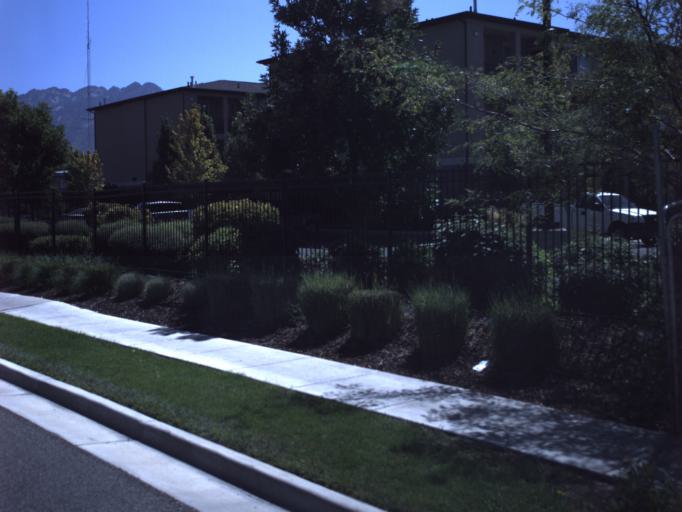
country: US
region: Utah
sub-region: Salt Lake County
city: Centerfield
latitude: 40.6998
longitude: -111.8850
